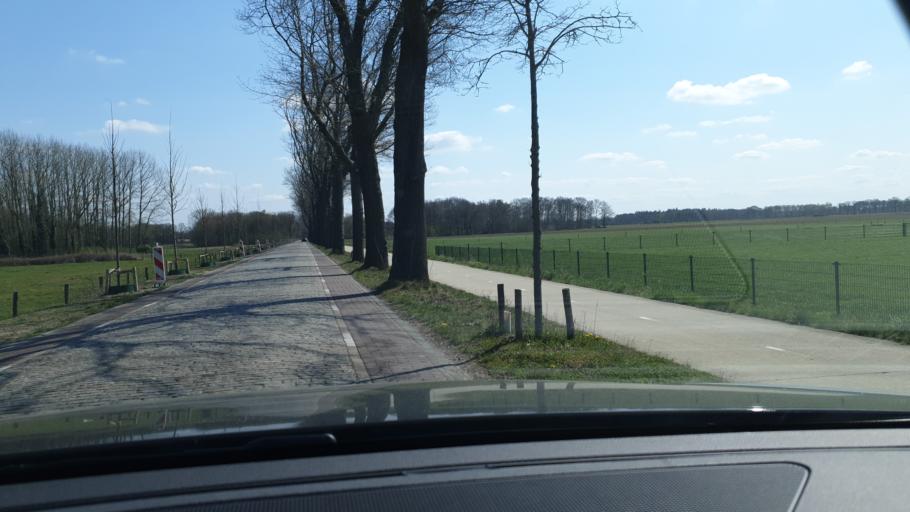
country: NL
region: North Brabant
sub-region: Gemeente Bladel en Netersel
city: Bladel
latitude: 51.4017
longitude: 5.2229
